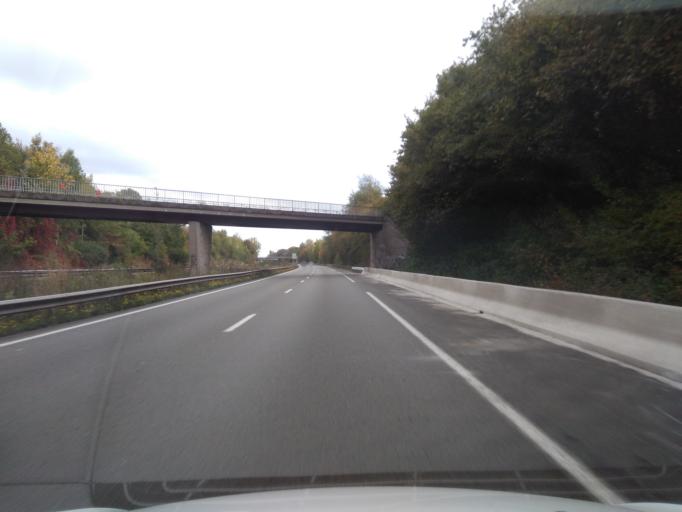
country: FR
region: Nord-Pas-de-Calais
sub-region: Departement du Nord
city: Saultain
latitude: 50.3408
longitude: 3.5666
